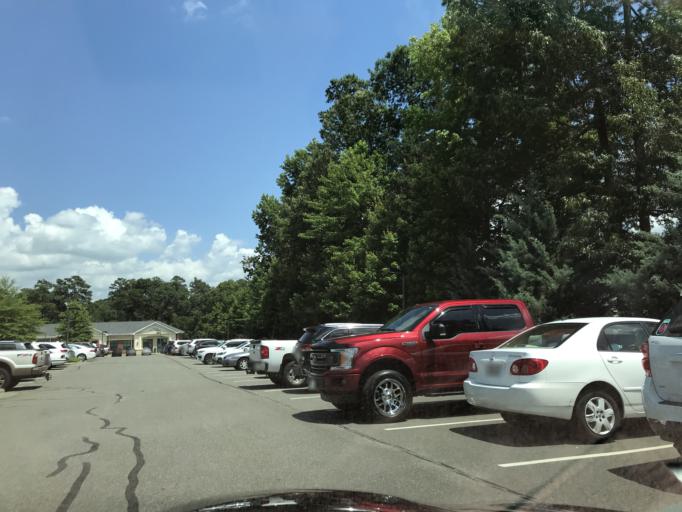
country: US
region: North Carolina
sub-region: Wake County
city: West Raleigh
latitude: 35.8209
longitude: -78.6991
